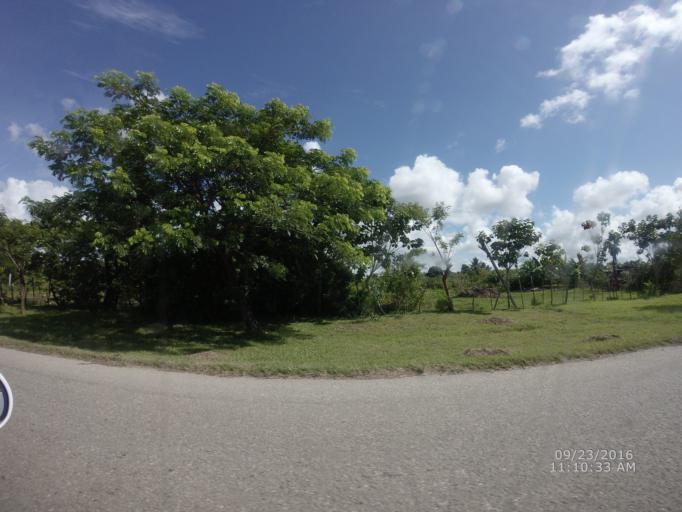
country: CU
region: La Habana
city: Arroyo Naranjo
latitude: 23.0211
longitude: -82.2575
